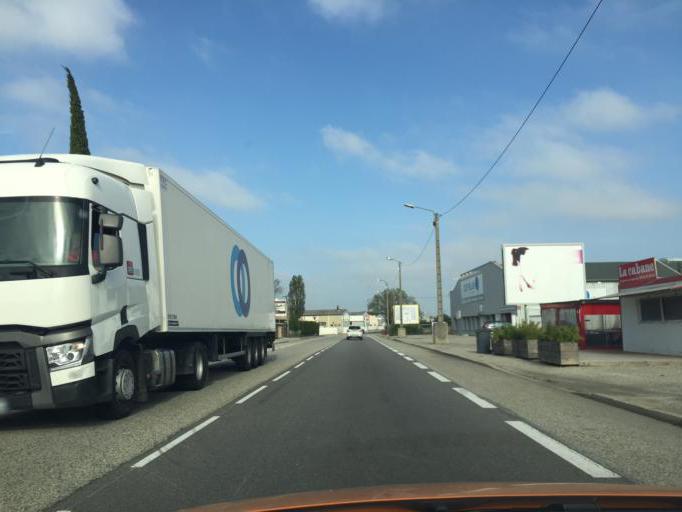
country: FR
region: Rhone-Alpes
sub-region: Departement de la Drome
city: Portes-les-Valence
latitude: 44.8951
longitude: 4.8837
